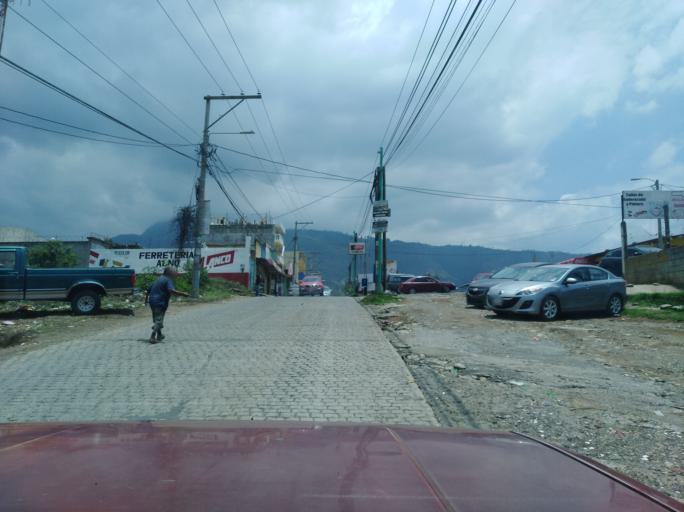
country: GT
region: Guatemala
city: Villa Nueva
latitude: 14.5285
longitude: -90.6225
